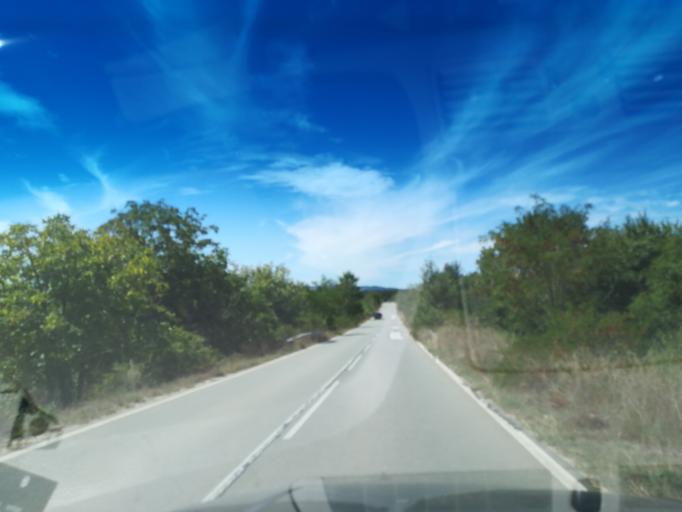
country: BG
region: Plovdiv
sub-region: Obshtina Suedinenie
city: Suedinenie
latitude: 42.3992
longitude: 24.5478
